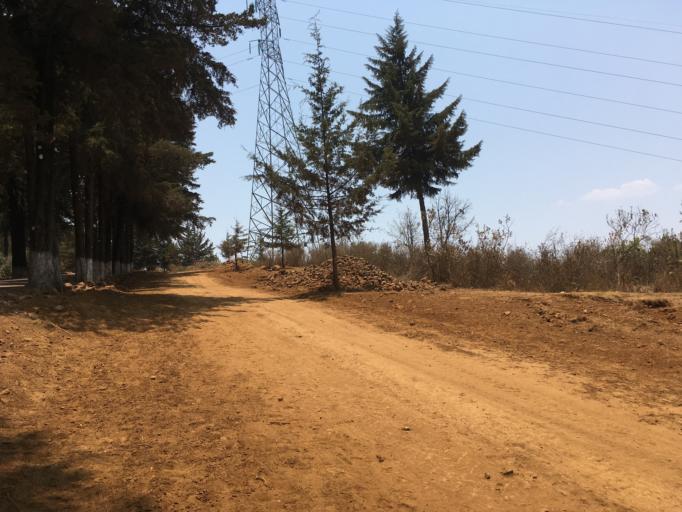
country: MX
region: Michoacan
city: Patzcuaro
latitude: 19.5154
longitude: -101.6276
